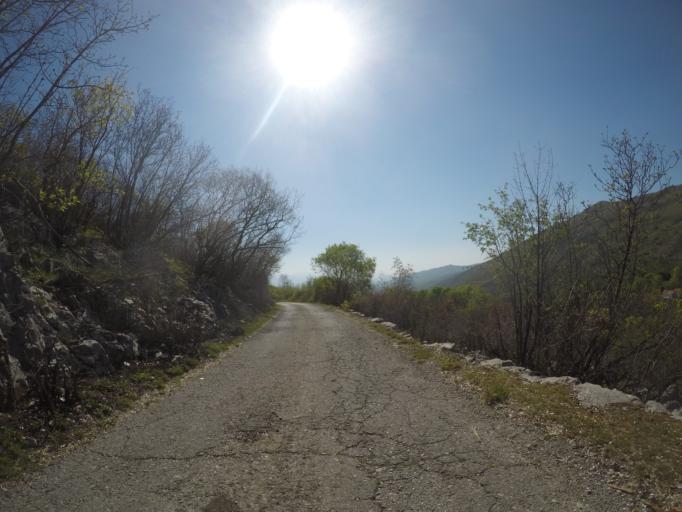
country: ME
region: Danilovgrad
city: Danilovgrad
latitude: 42.5170
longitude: 19.0609
